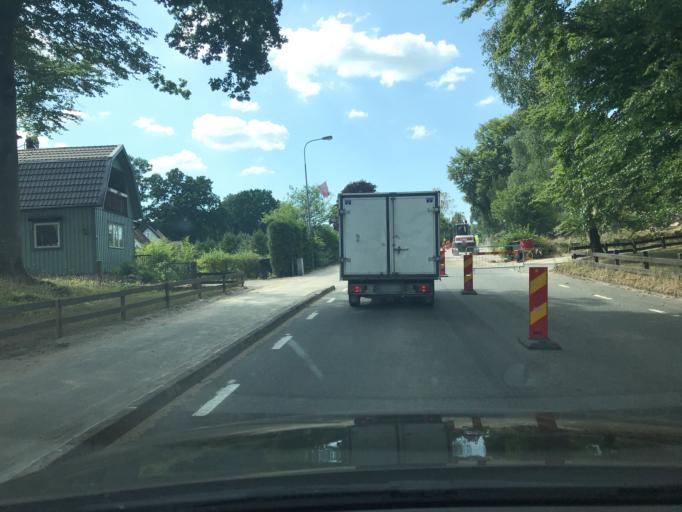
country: SE
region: Skane
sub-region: Hassleholms Kommun
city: Hastveda
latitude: 56.2862
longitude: 13.9229
